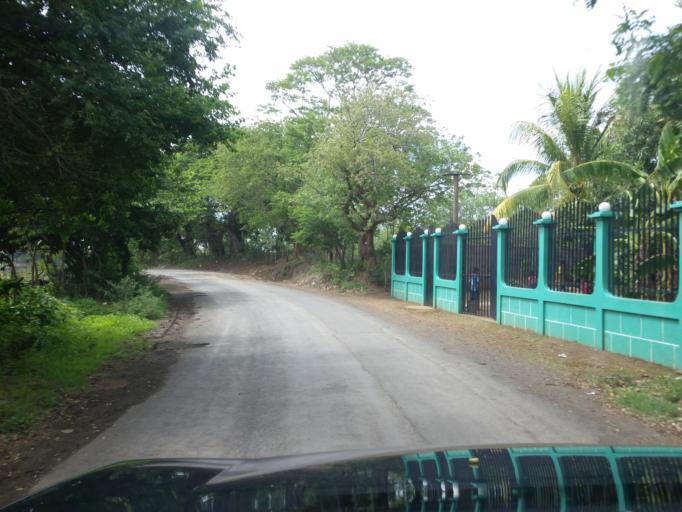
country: NI
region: Masaya
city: Ticuantepe
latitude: 12.0795
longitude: -86.1891
